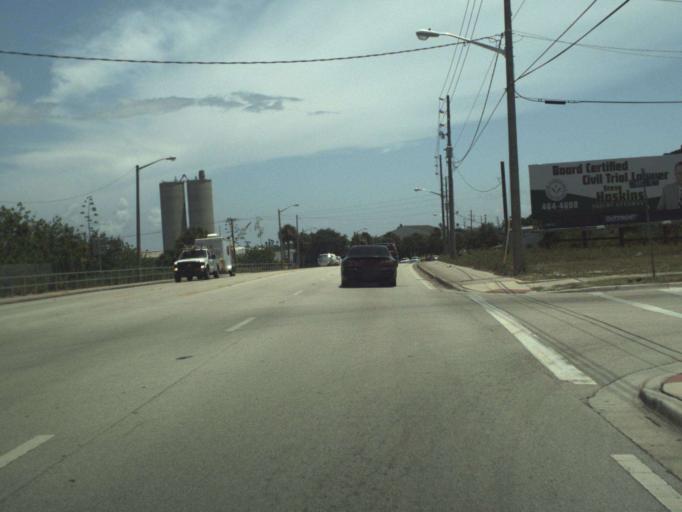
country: US
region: Florida
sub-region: Saint Lucie County
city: Fort Pierce
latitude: 27.4635
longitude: -80.3302
